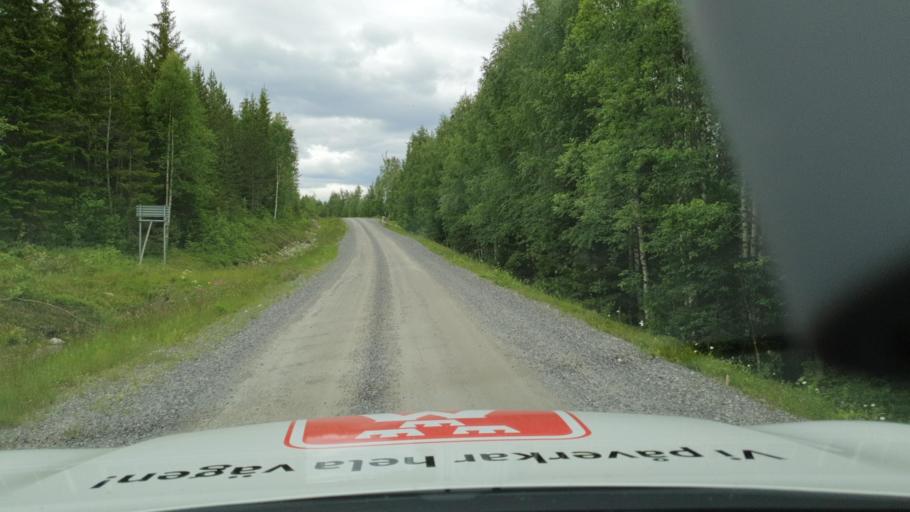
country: SE
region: Vaesterbotten
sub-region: Bjurholms Kommun
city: Bjurholm
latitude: 63.7578
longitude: 19.3677
